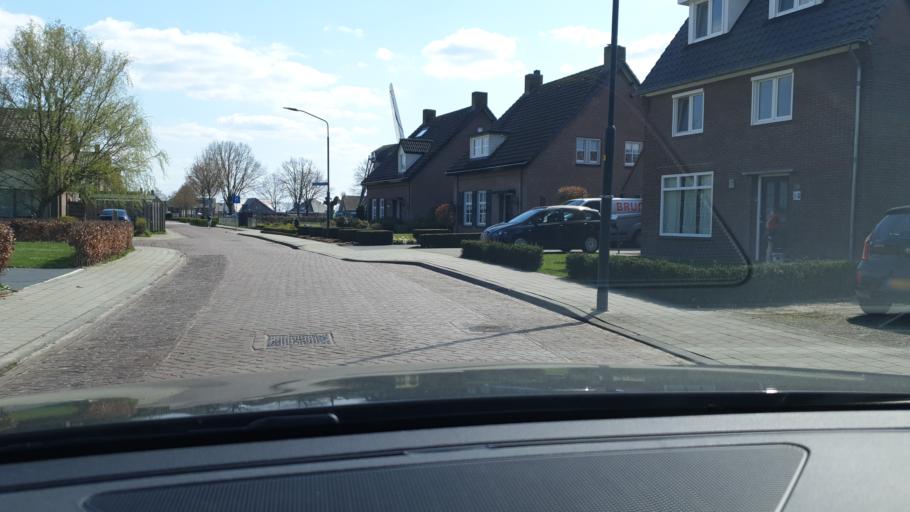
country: NL
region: North Brabant
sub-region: Gemeente Bladel en Netersel
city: Bladel
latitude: 51.3659
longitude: 5.2517
